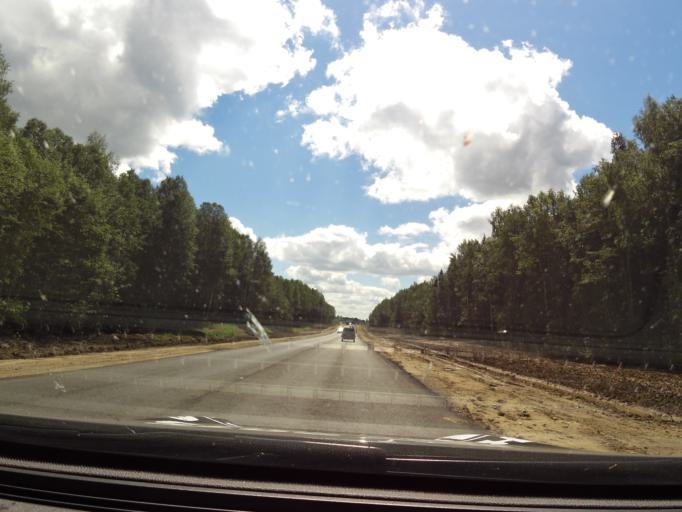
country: RU
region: Vologda
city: Molochnoye
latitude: 59.3521
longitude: 39.6767
